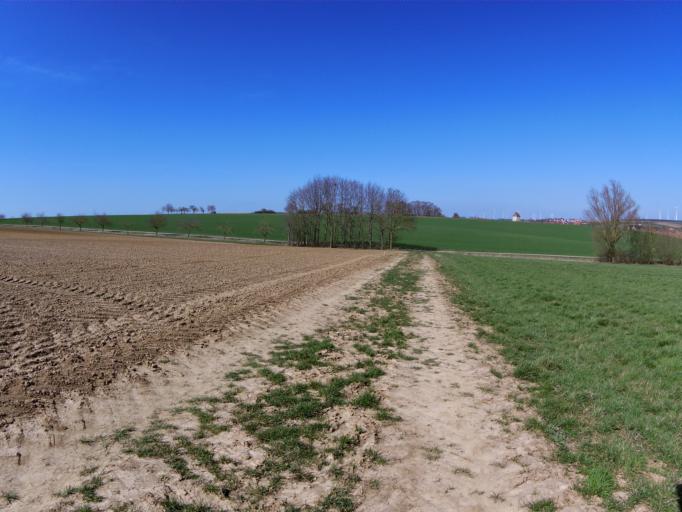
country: DE
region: Bavaria
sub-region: Regierungsbezirk Unterfranken
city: Prosselsheim
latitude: 49.8532
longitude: 10.1246
